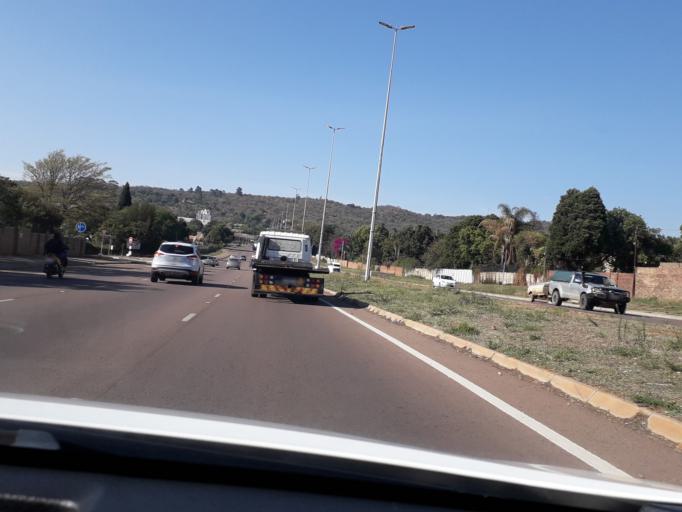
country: ZA
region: Gauteng
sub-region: City of Tshwane Metropolitan Municipality
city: Pretoria
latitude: -25.7602
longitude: 28.3232
